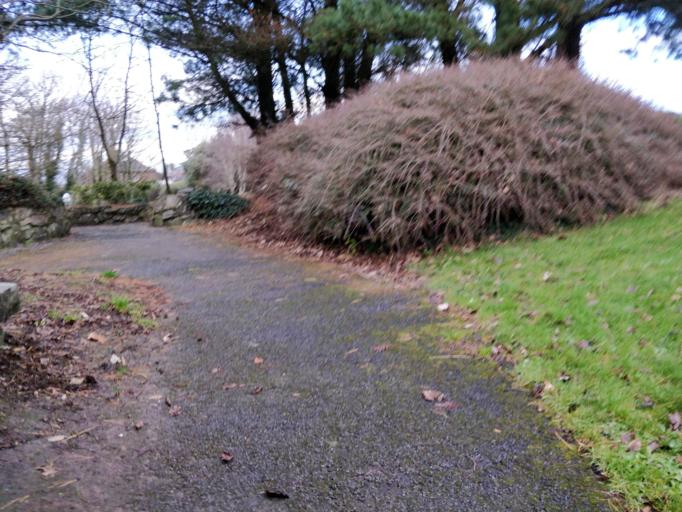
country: IE
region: Connaught
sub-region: County Galway
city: Gaillimh
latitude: 53.2584
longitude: -9.0860
